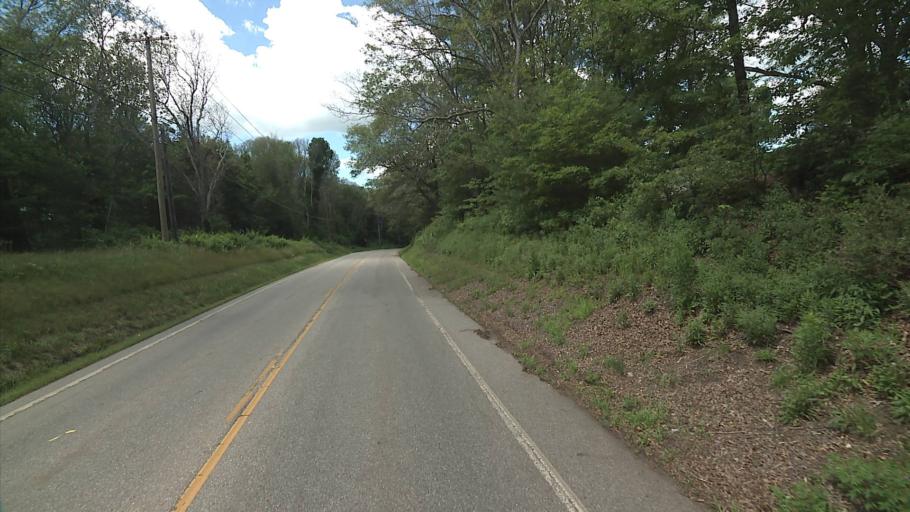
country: US
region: Connecticut
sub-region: New London County
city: Pawcatuck
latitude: 41.4223
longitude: -71.8658
